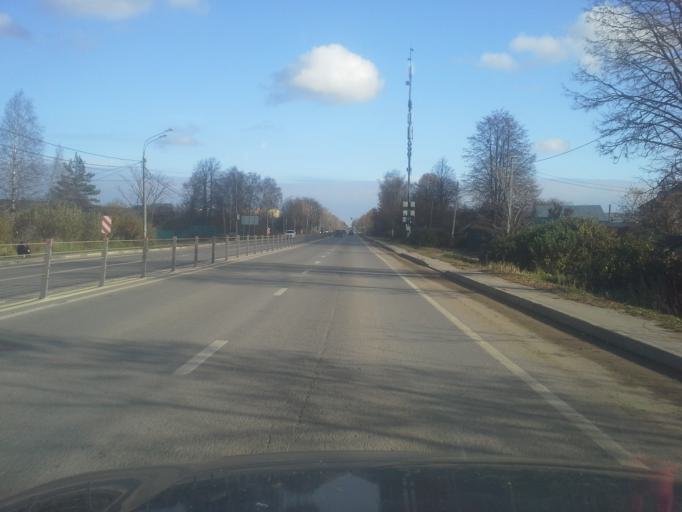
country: RU
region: Moskovskaya
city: Krasnoznamensk
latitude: 55.6344
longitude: 37.0377
